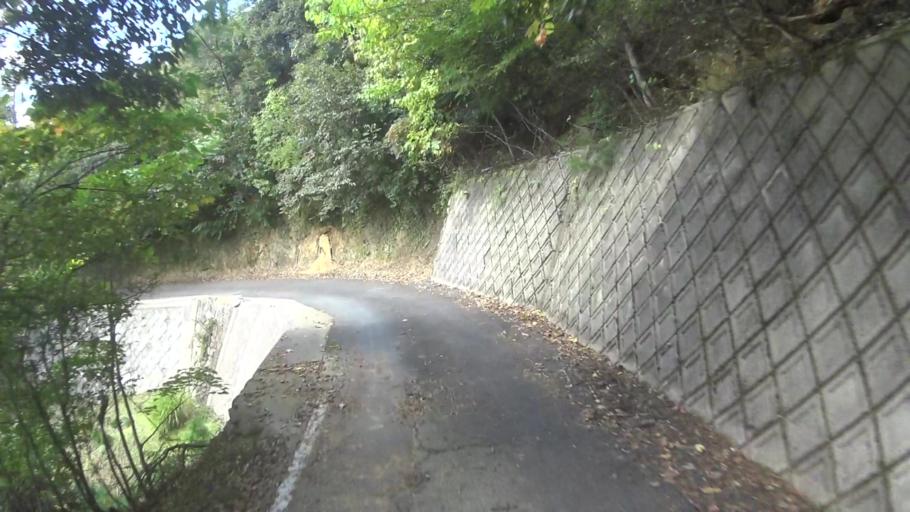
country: JP
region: Hyogo
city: Toyooka
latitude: 35.6103
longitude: 134.9939
